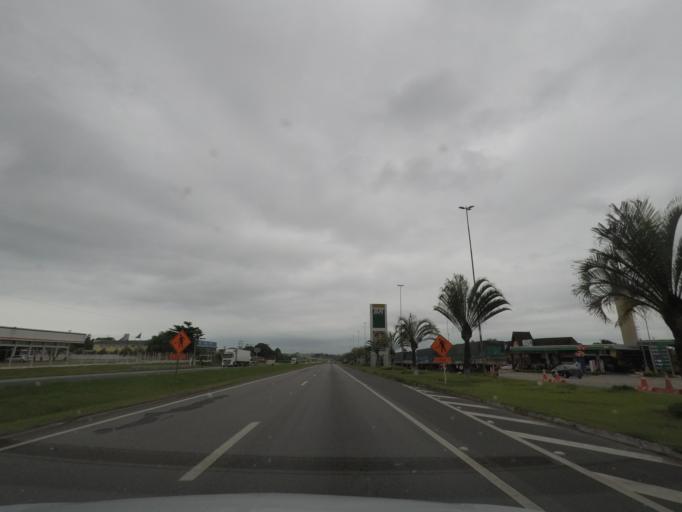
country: BR
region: Sao Paulo
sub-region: Registro
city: Registro
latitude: -24.4755
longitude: -47.8272
